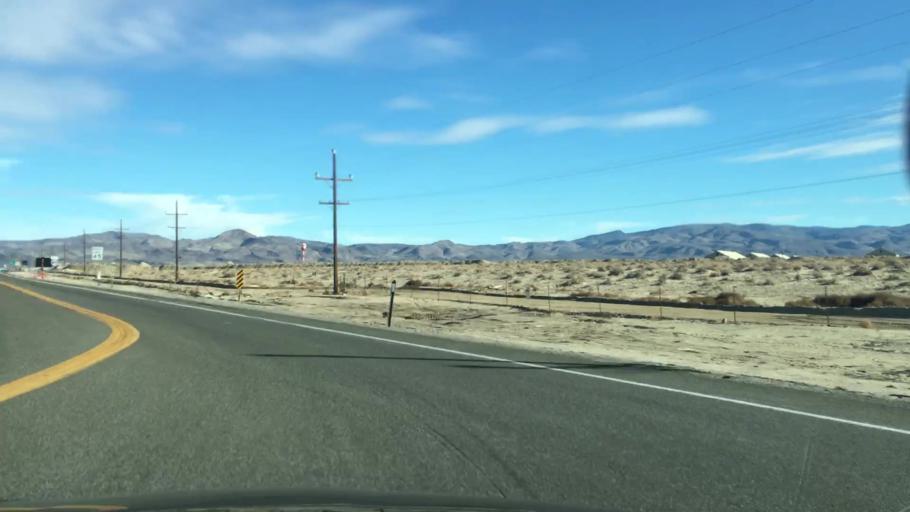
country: US
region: Nevada
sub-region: Mineral County
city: Hawthorne
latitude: 38.5245
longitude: -118.6108
